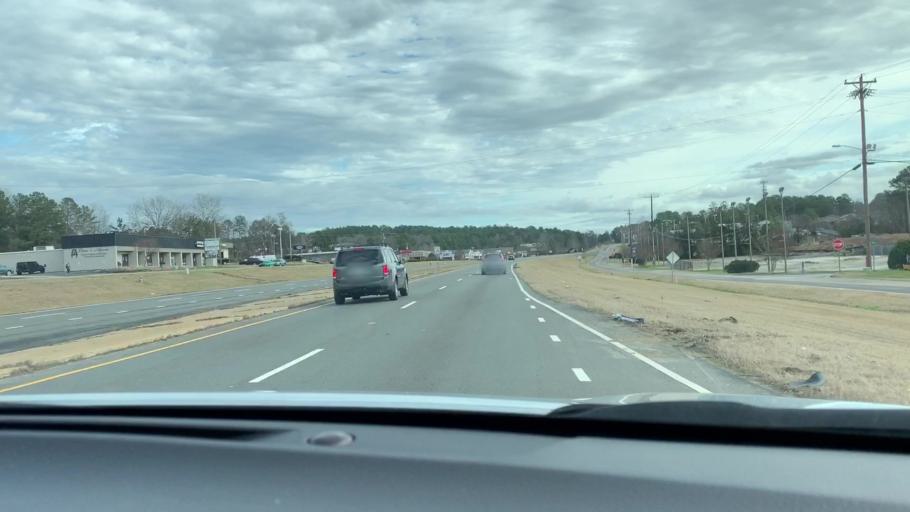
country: US
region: North Carolina
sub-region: Durham County
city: Durham
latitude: 35.9704
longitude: -78.9543
